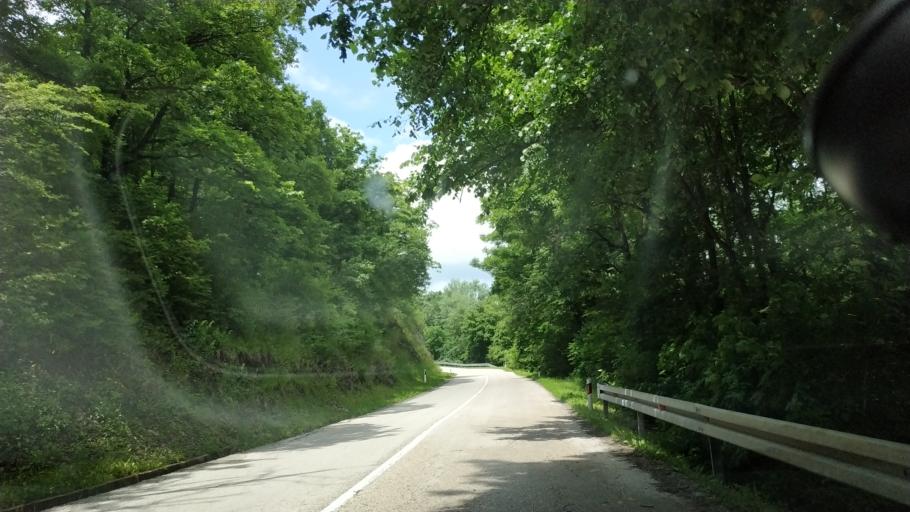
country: RS
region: Central Serbia
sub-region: Borski Okrug
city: Bor
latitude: 44.0611
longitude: 22.0433
